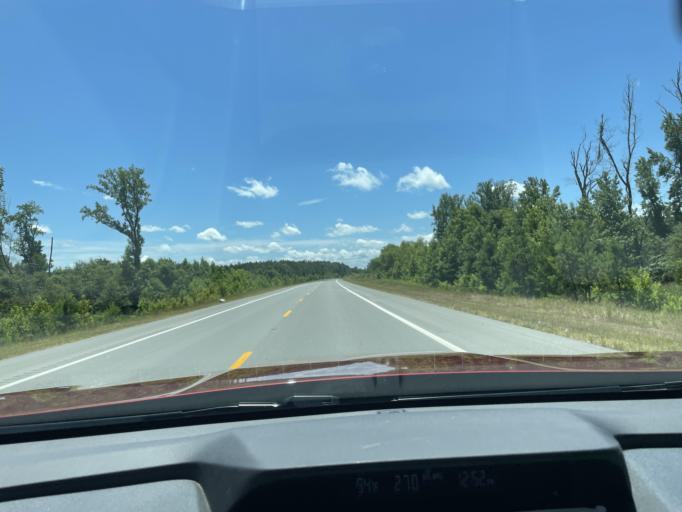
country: US
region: Arkansas
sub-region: Lincoln County
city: Star City
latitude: 33.9215
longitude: -91.8852
